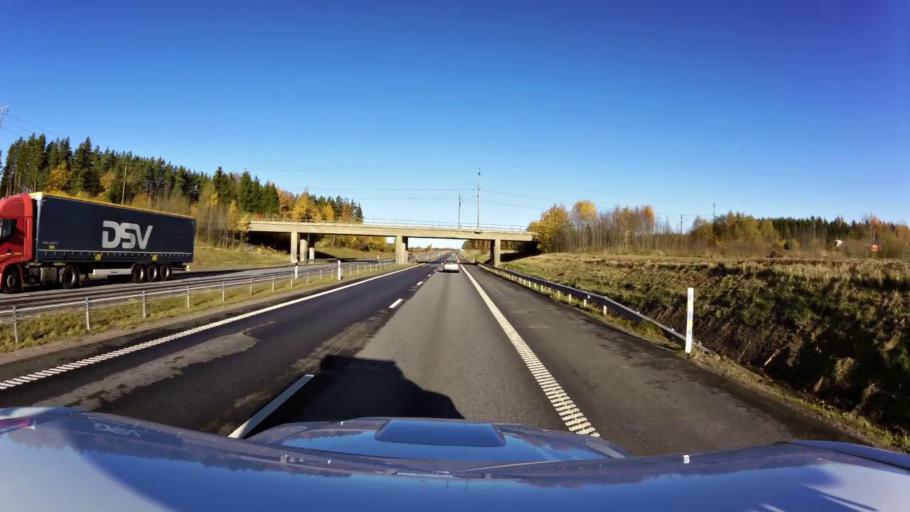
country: SE
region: OEstergoetland
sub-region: Linkopings Kommun
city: Malmslatt
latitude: 58.4144
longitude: 15.5456
